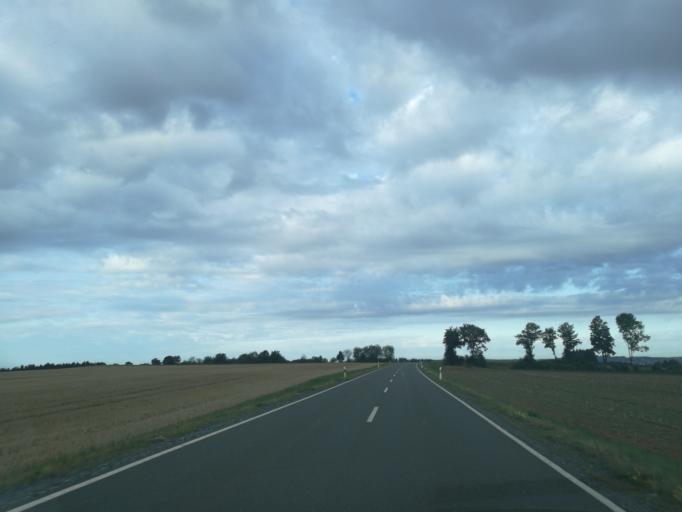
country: DE
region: Bavaria
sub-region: Upper Franconia
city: Gattendorf
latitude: 50.2942
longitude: 11.9976
